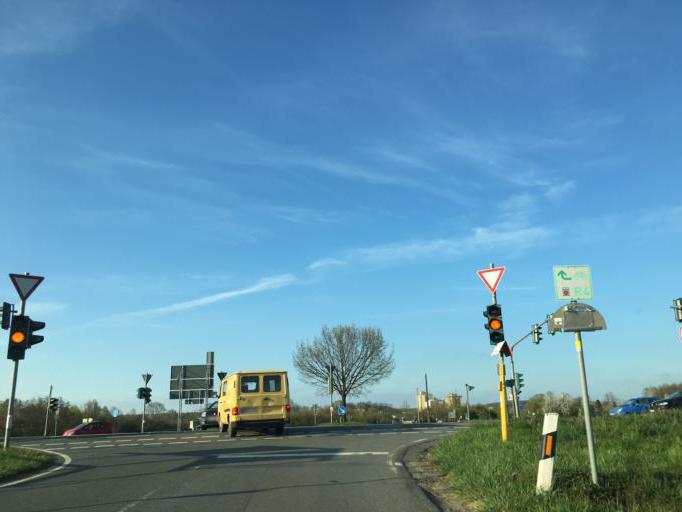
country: DE
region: Hesse
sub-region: Regierungsbezirk Darmstadt
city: Maintal
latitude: 50.1368
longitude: 8.8026
